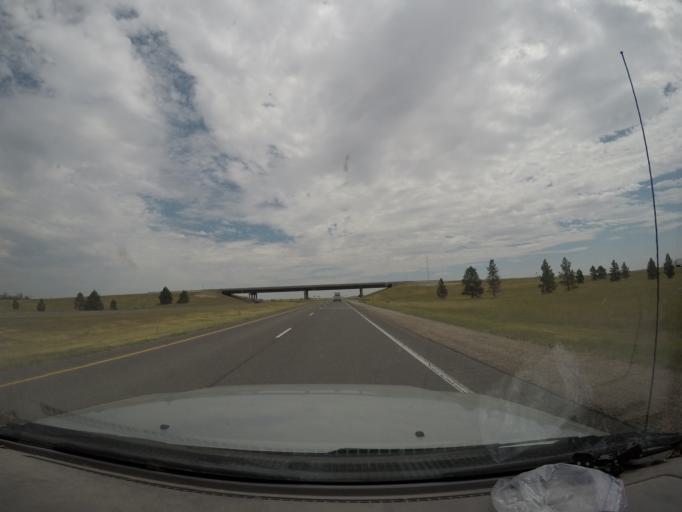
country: US
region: Wyoming
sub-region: Laramie County
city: Pine Bluffs
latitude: 41.1918
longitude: -103.8947
